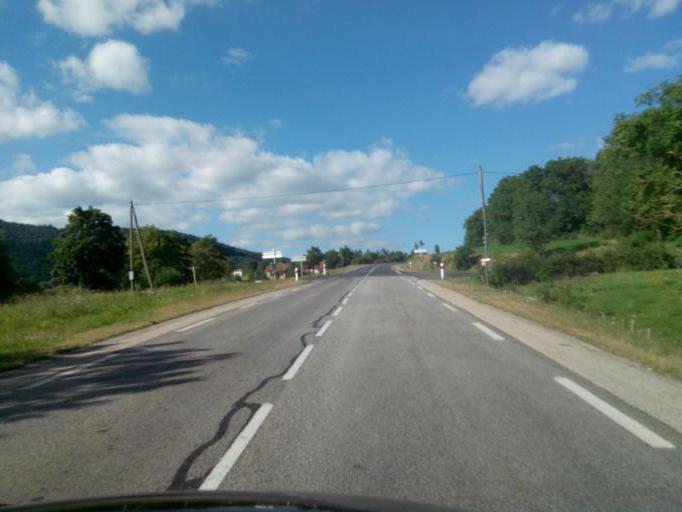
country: FR
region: Auvergne
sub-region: Departement de la Haute-Loire
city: Saint-Paulien
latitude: 45.1551
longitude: 3.8244
